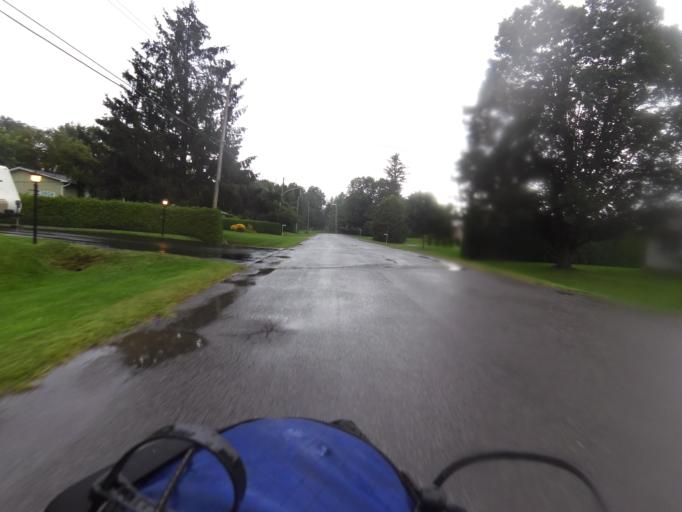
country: CA
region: Ontario
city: Ottawa
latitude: 45.2330
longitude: -75.4830
